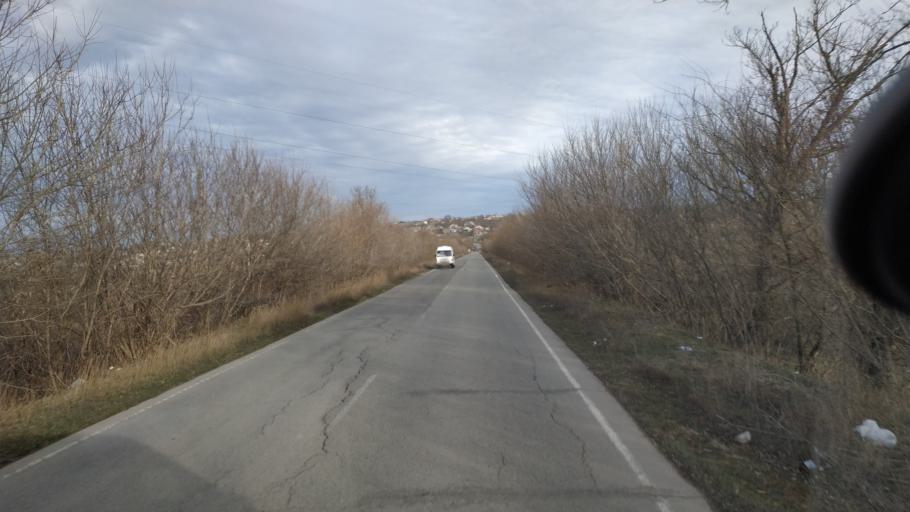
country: MD
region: Chisinau
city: Vadul lui Voda
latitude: 47.1102
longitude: 29.0611
